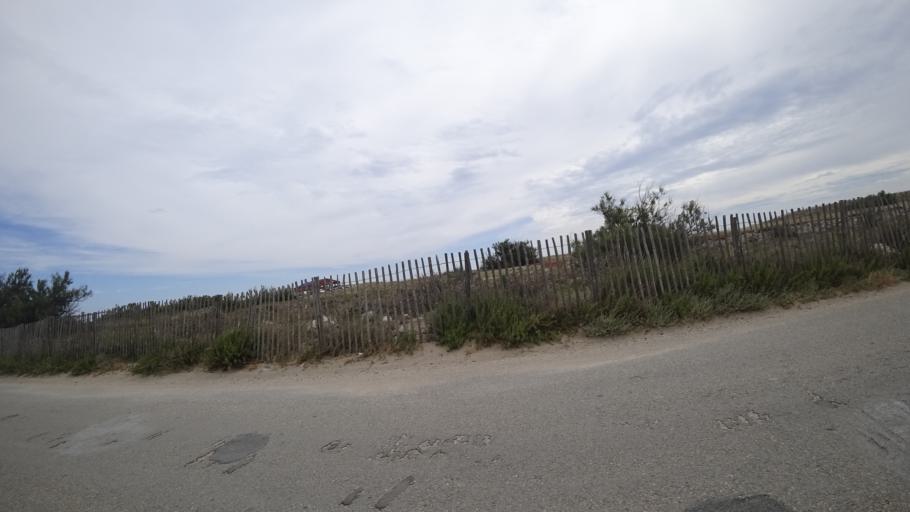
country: FR
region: Languedoc-Roussillon
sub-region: Departement de l'Aude
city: Leucate
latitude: 42.8878
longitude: 3.0501
